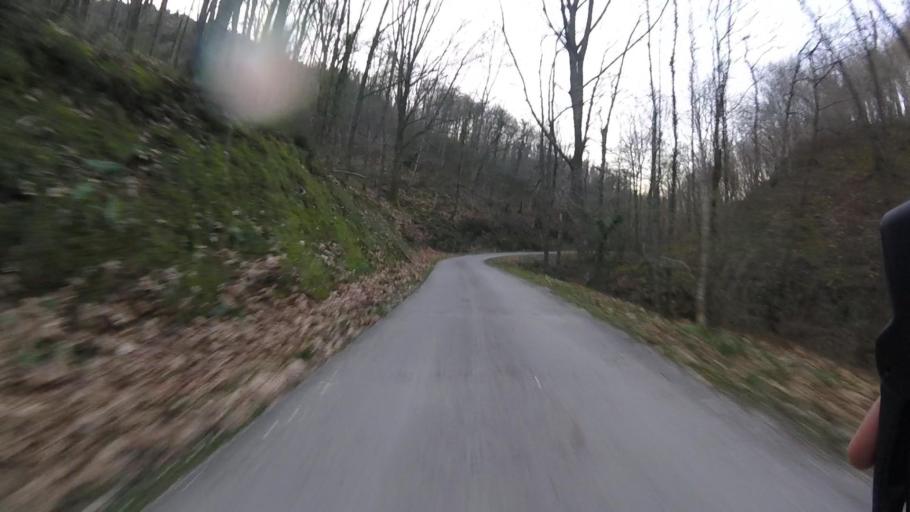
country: ES
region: Basque Country
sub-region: Provincia de Guipuzcoa
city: Errenteria
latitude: 43.2722
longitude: -1.8647
